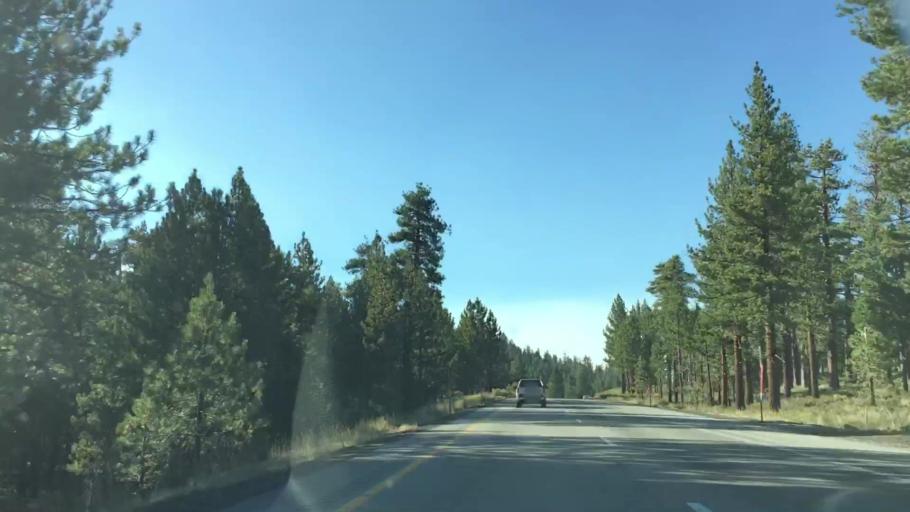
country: US
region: California
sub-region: Mono County
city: Mammoth Lakes
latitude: 37.6740
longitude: -118.9375
